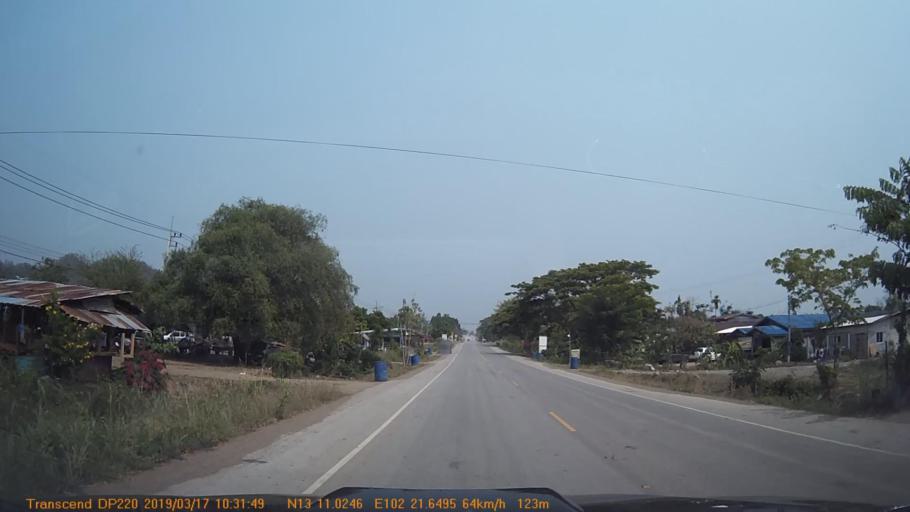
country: TH
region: Chanthaburi
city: Soi Dao
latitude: 13.1841
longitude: 102.3607
